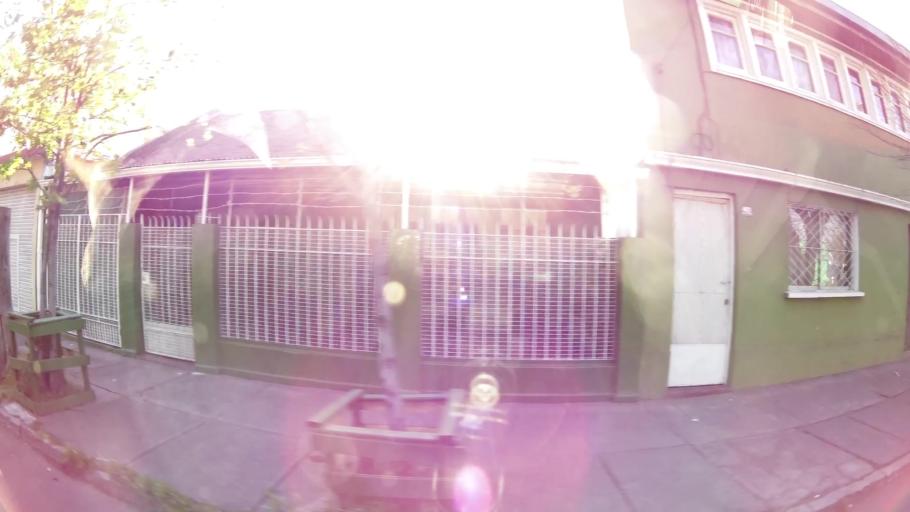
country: CL
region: Santiago Metropolitan
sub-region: Provincia de Santiago
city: Santiago
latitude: -33.3843
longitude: -70.6719
